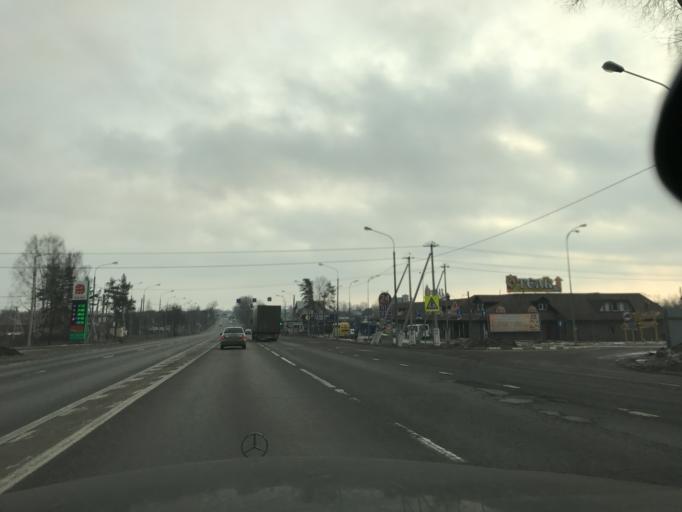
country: RU
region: Vladimir
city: Pokrov
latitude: 55.9144
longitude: 39.1517
